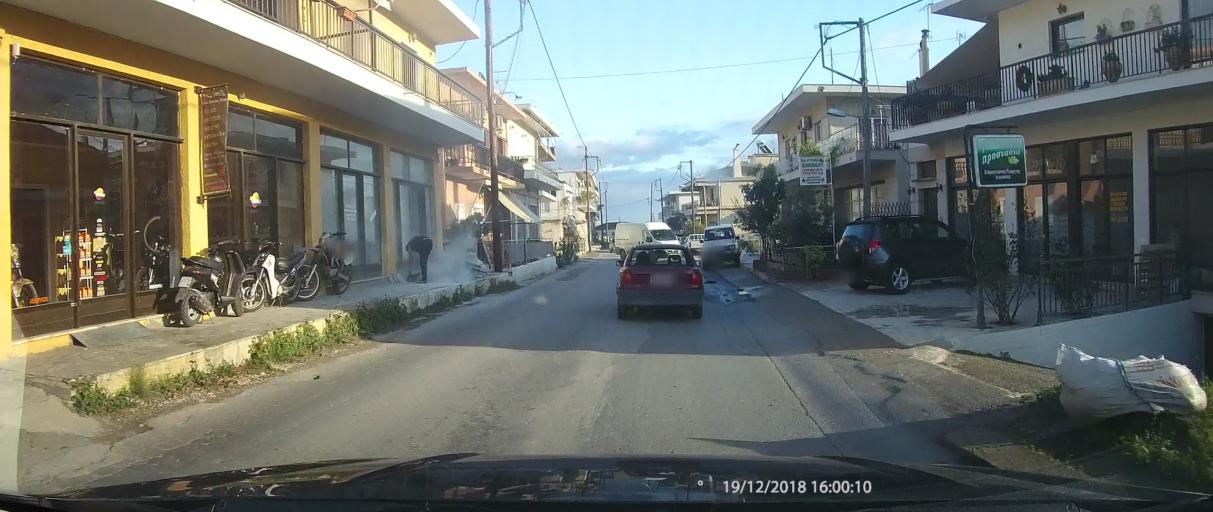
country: GR
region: Peloponnese
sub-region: Nomos Lakonias
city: Skala
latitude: 36.8551
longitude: 22.6766
